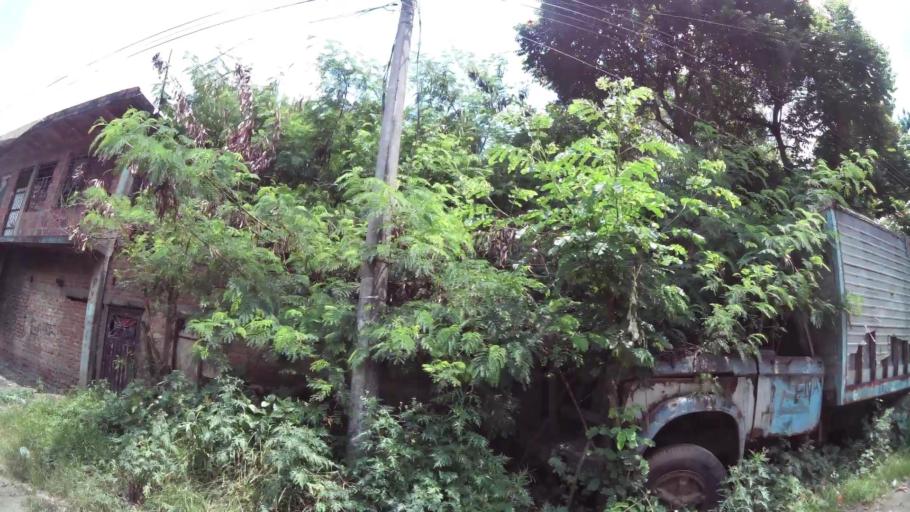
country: CO
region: Valle del Cauca
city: Cali
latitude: 3.4514
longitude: -76.4765
